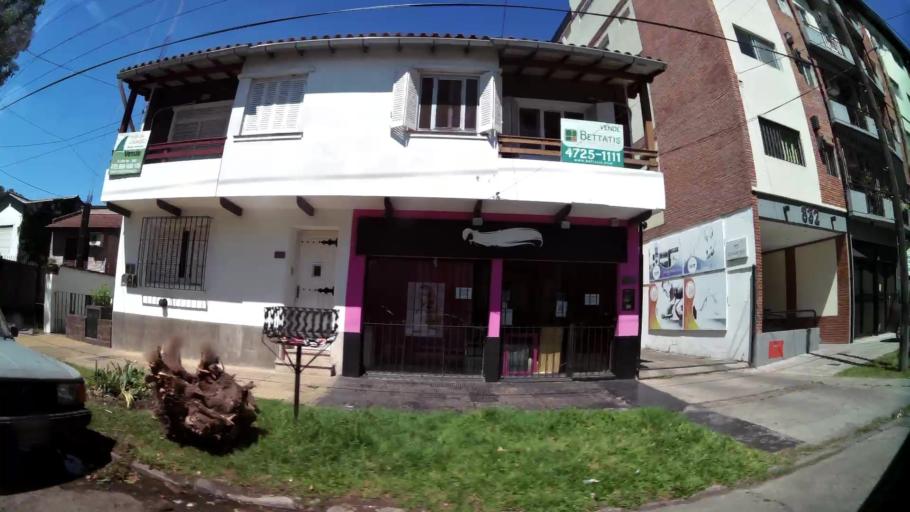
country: AR
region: Buenos Aires
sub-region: Partido de Tigre
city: Tigre
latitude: -34.4282
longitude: -58.5722
